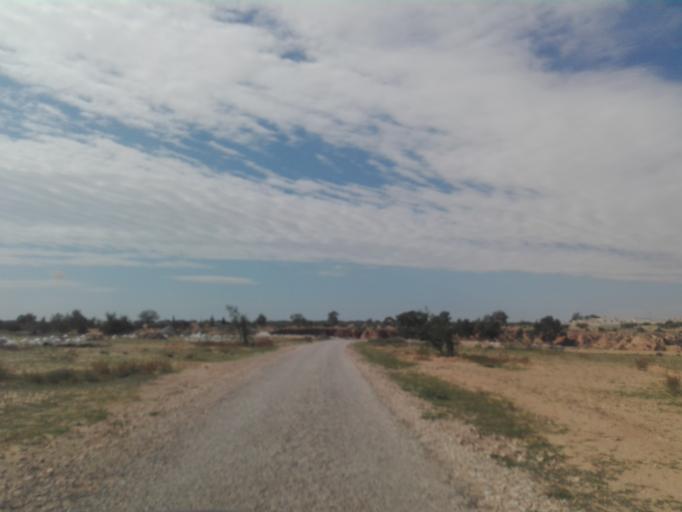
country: TN
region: Safaqis
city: Sfax
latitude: 34.6874
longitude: 10.5615
